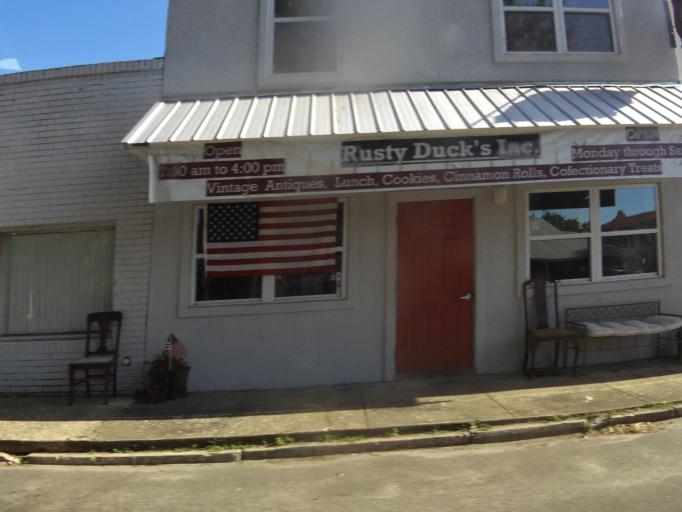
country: US
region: Florida
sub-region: Putnam County
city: Palatka
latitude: 29.6453
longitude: -81.6358
